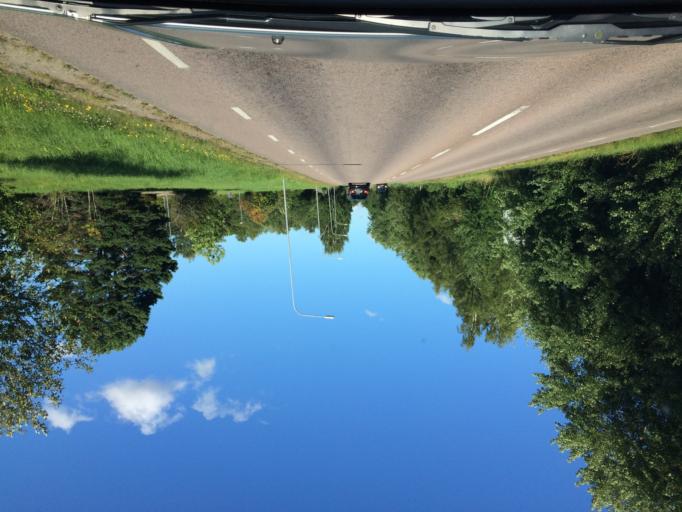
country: SE
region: Vaestmanland
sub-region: Vasteras
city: Vasteras
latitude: 59.6024
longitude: 16.5887
